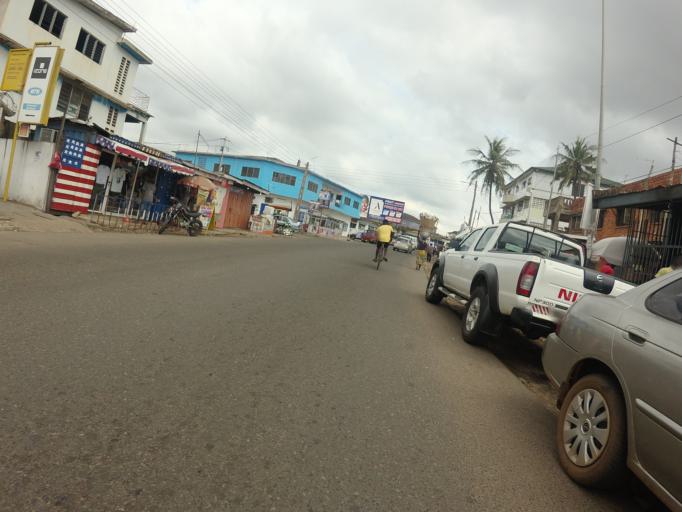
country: GH
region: Greater Accra
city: Accra
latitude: 5.5897
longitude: -0.2072
